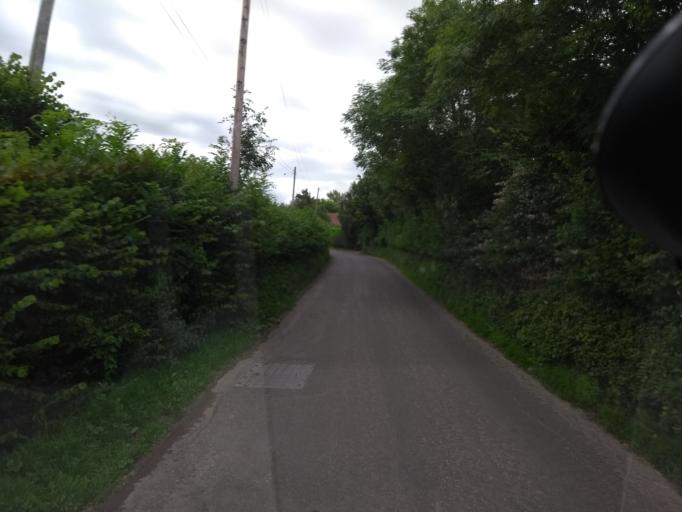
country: GB
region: England
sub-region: Somerset
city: Bishops Lydeard
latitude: 51.1864
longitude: -3.1550
